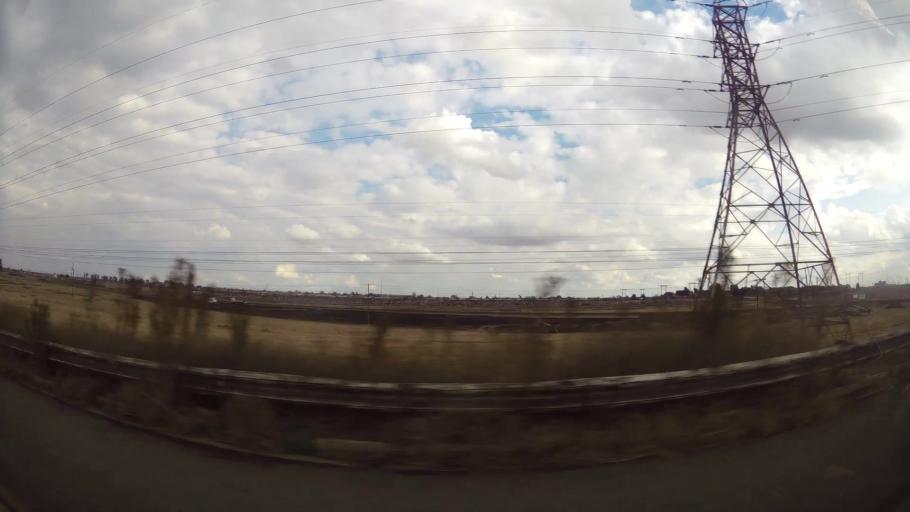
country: ZA
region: Orange Free State
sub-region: Fezile Dabi District Municipality
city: Sasolburg
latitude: -26.8342
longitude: 27.8639
